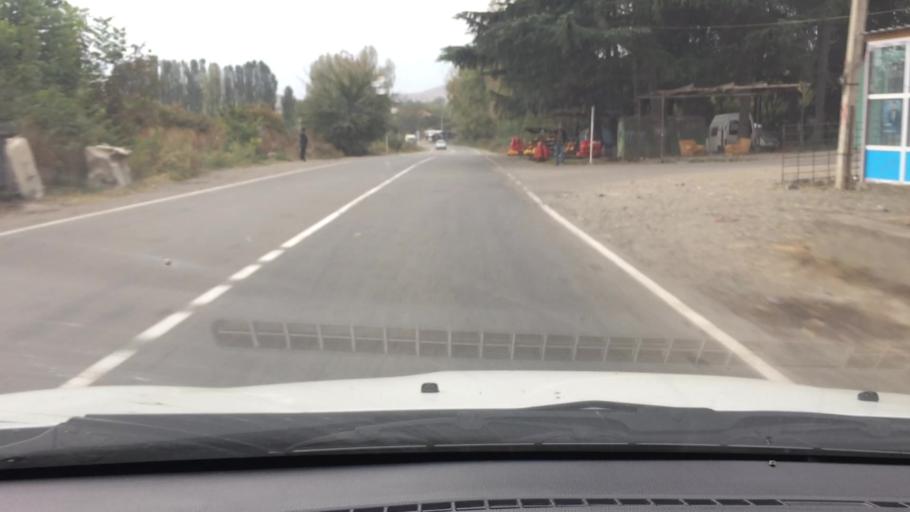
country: AM
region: Tavush
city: Bagratashen
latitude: 41.2953
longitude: 44.7887
